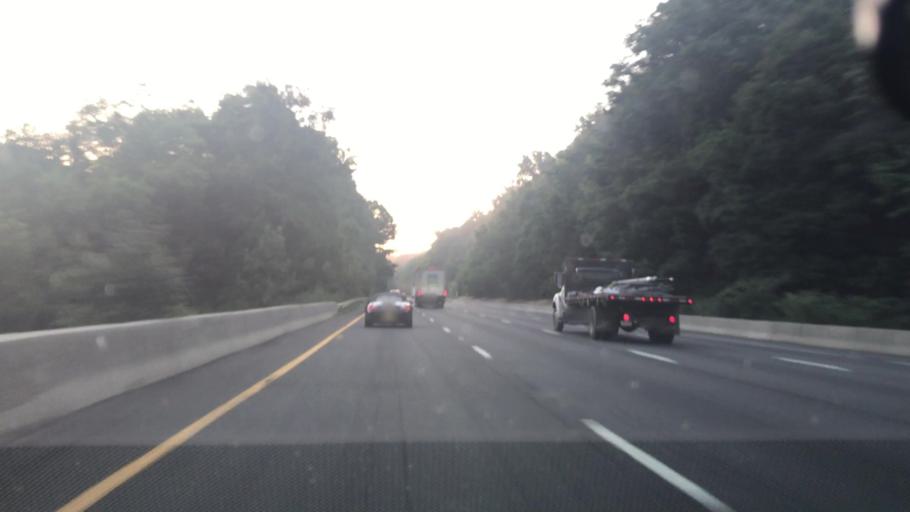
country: US
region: New Jersey
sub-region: Somerset County
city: Bedminster
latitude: 40.6708
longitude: -74.6249
